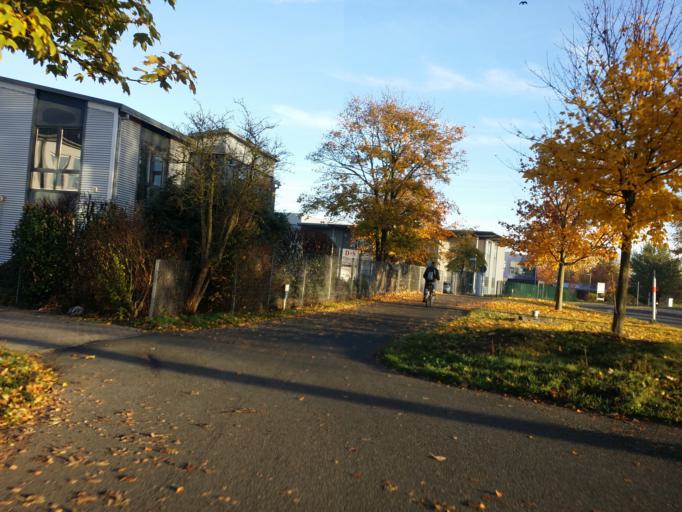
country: DE
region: Lower Saxony
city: Stuhr
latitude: 53.0202
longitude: 8.7907
